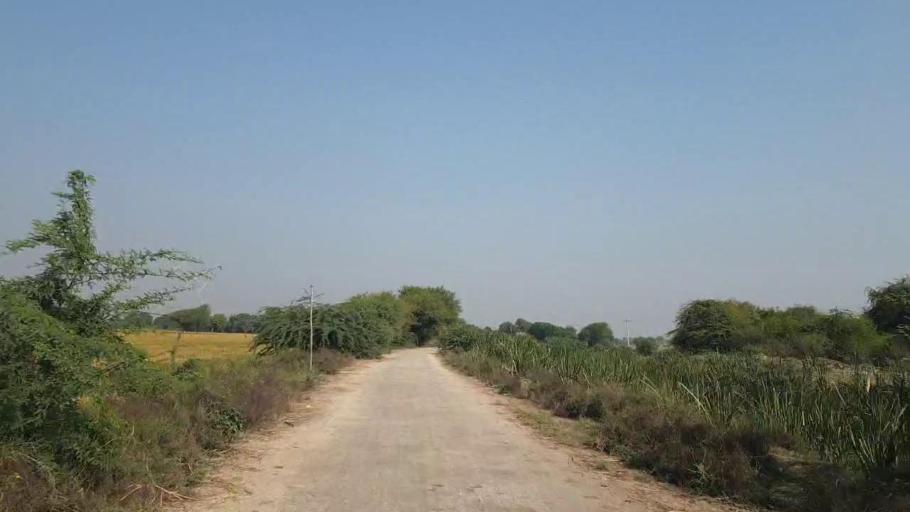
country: PK
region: Sindh
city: Matli
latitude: 24.9983
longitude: 68.6219
